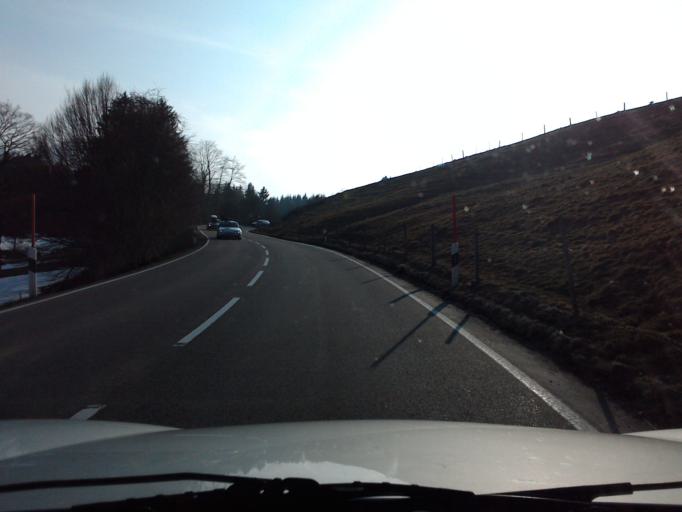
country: DE
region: Bavaria
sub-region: Swabia
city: Oberstdorf
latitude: 47.4110
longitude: 10.2569
